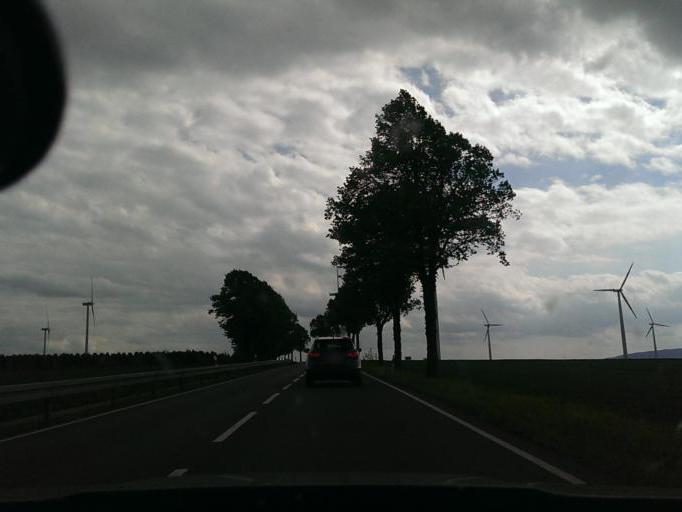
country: DE
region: Lower Saxony
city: Nordstemmen
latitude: 52.1993
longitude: 9.7470
